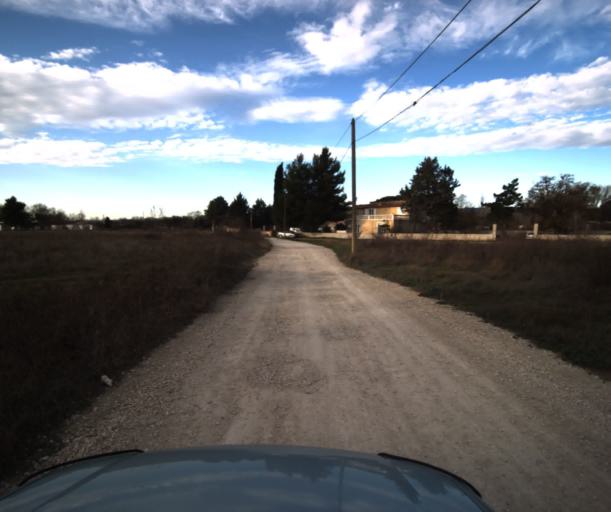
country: FR
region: Provence-Alpes-Cote d'Azur
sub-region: Departement des Bouches-du-Rhone
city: Meyrargues
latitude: 43.6635
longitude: 5.5300
